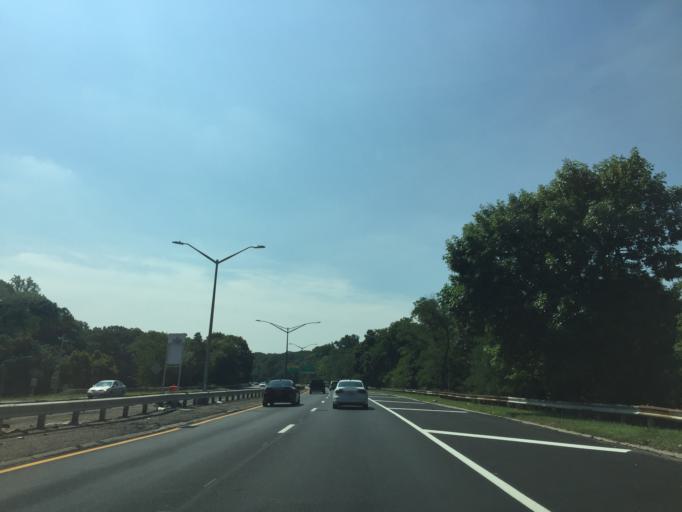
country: US
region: New York
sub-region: Nassau County
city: Bellerose Terrace
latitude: 40.7340
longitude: -73.7668
